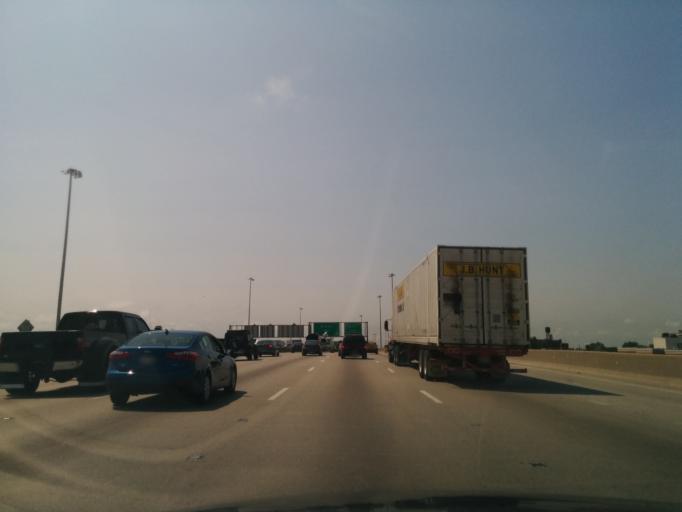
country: US
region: Illinois
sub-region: Cook County
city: Chicago
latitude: 41.8623
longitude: -87.6447
